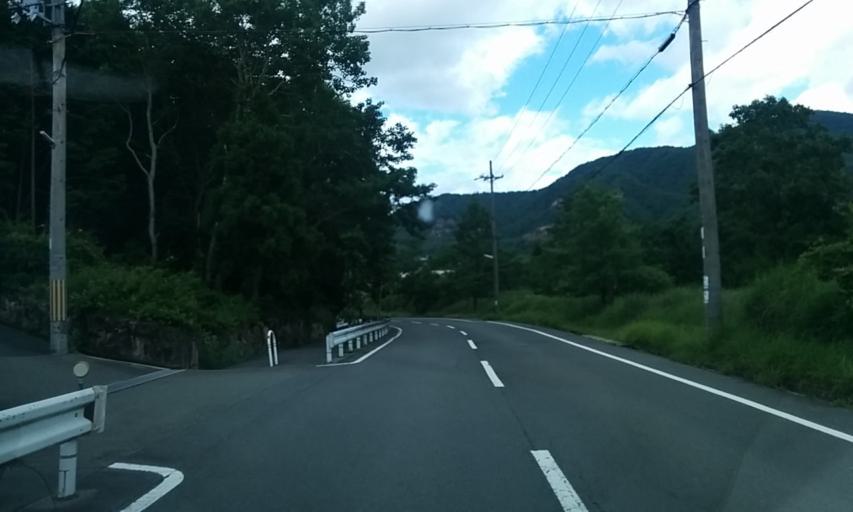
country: JP
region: Kyoto
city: Kameoka
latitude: 35.0076
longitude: 135.4319
